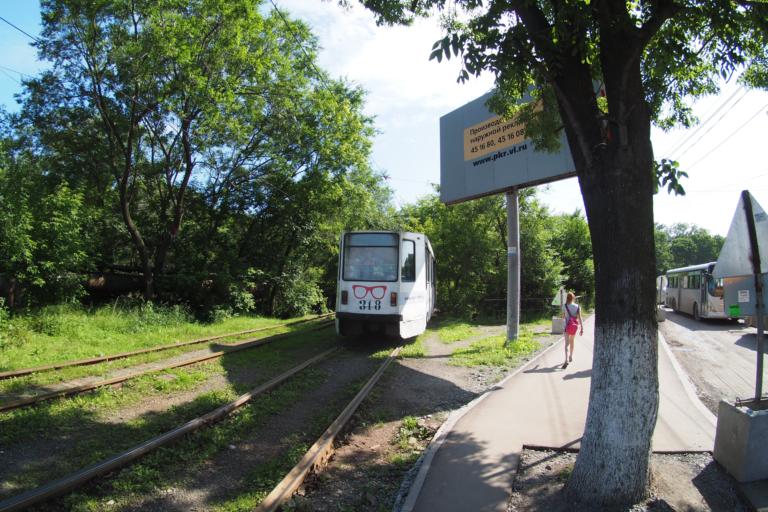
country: RU
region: Primorskiy
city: Vladivostok
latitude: 43.1046
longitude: 131.9380
